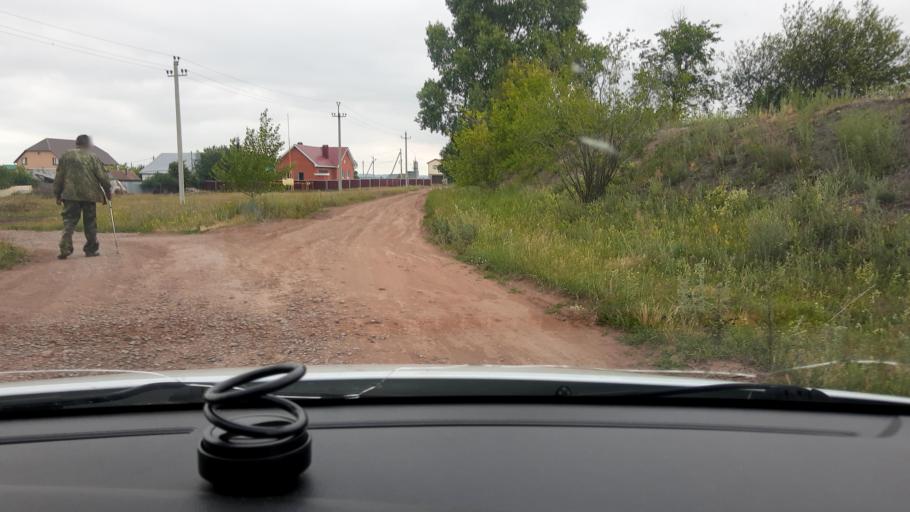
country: RU
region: Bashkortostan
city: Avdon
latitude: 54.6406
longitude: 55.5674
